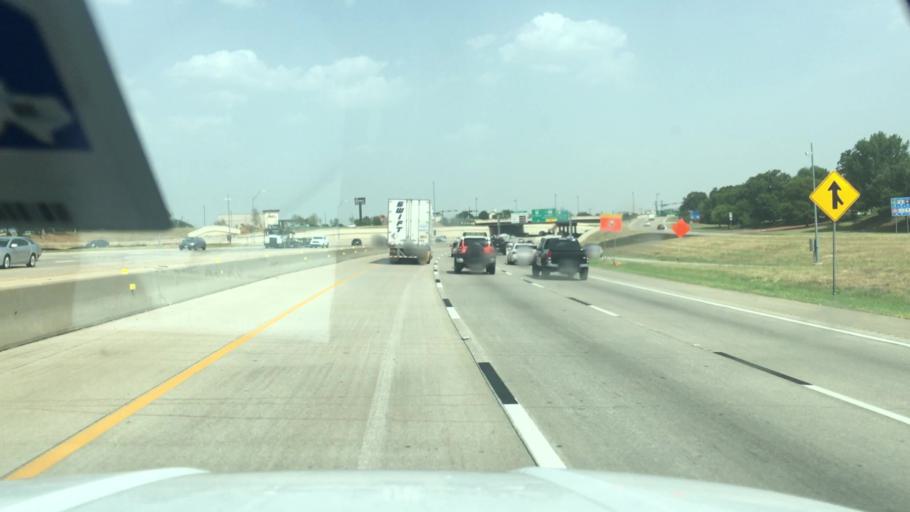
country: US
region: Texas
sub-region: Tarrant County
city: Grapevine
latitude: 32.9419
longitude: -97.1047
